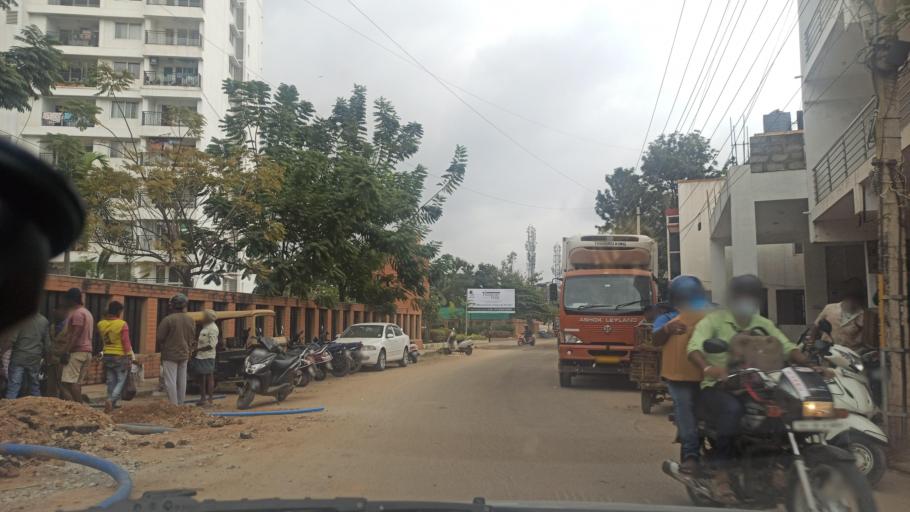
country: IN
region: Karnataka
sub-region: Bangalore Urban
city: Yelahanka
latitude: 13.0468
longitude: 77.6011
